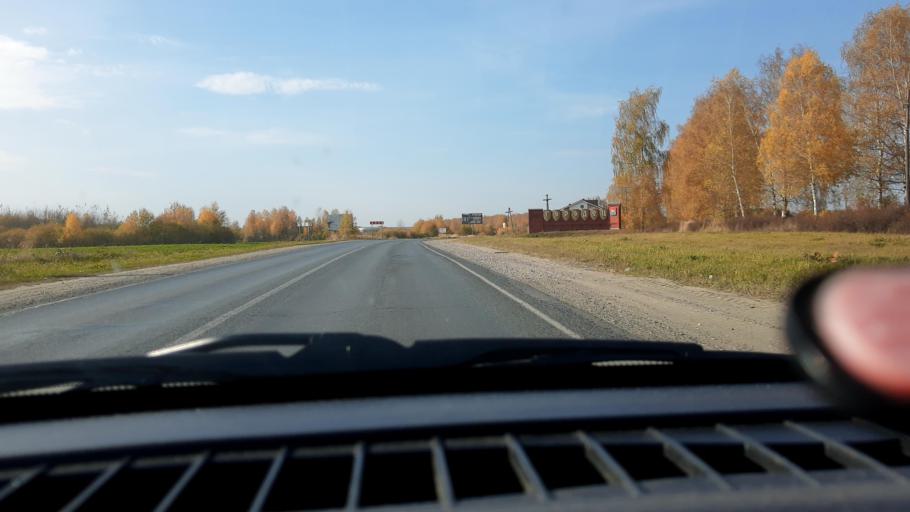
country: RU
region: Nizjnij Novgorod
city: Gorodets
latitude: 56.6387
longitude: 43.5098
